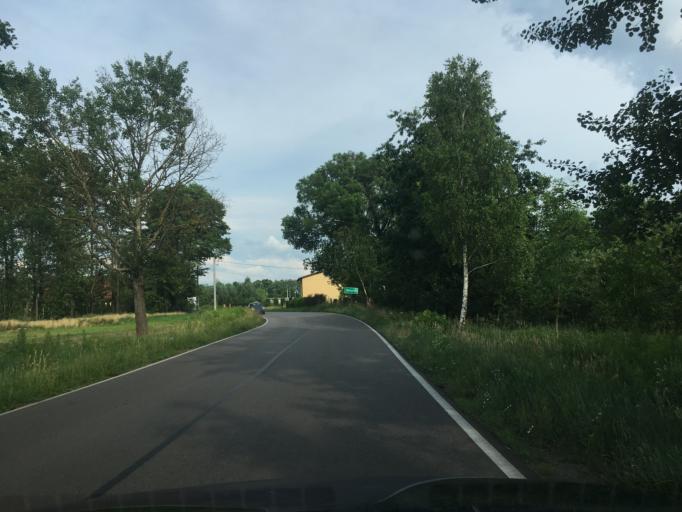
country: PL
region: Masovian Voivodeship
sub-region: Powiat wolominski
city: Radzymin
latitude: 52.4116
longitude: 21.2197
